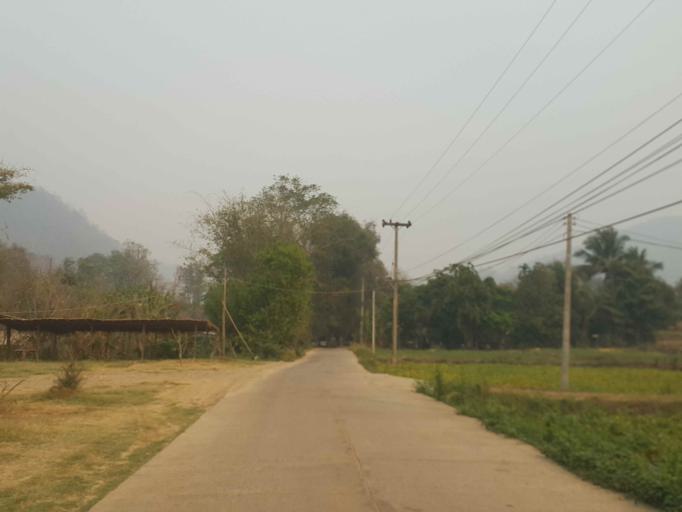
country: TH
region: Chiang Mai
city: Mae Taeng
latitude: 19.2193
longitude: 98.8506
